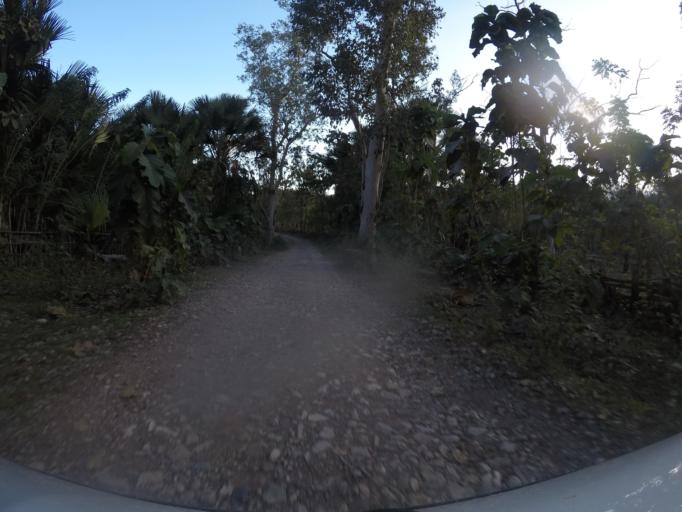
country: TL
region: Baucau
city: Venilale
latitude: -8.7224
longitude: 126.7091
